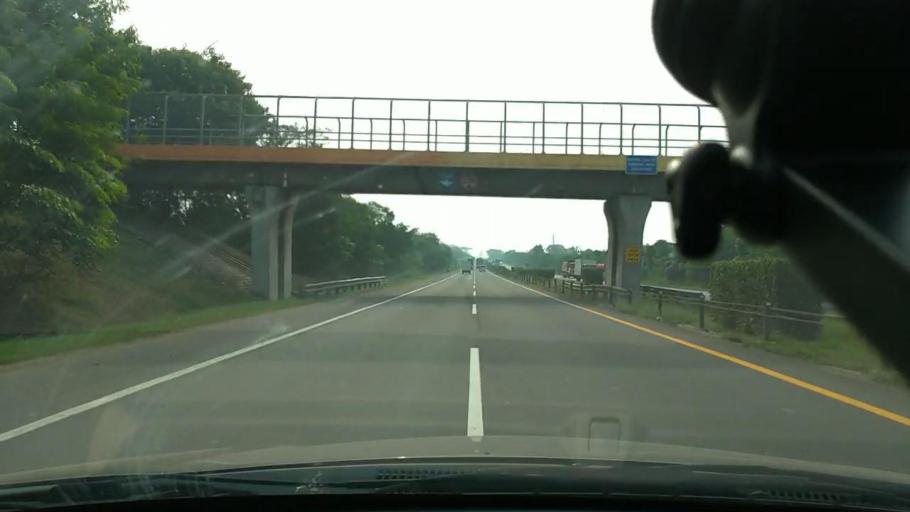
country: ID
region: Banten
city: Serang
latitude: -6.1110
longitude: 106.1819
